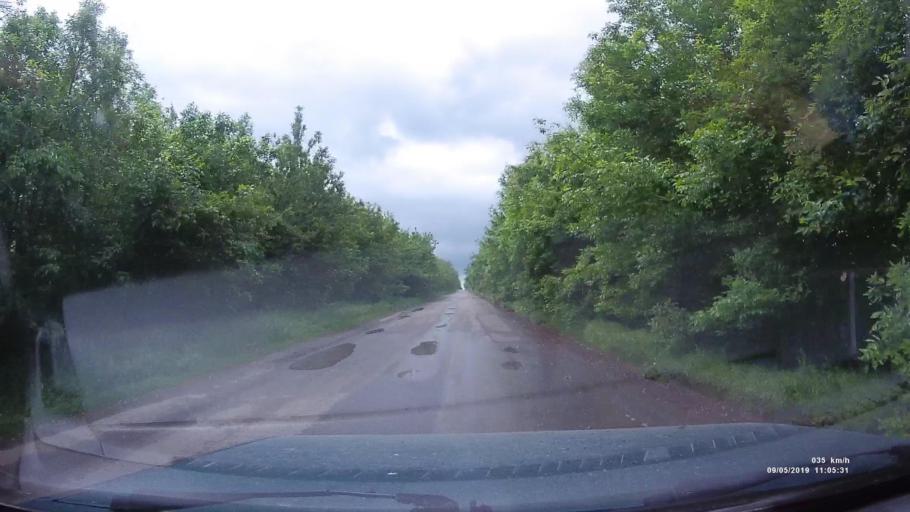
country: RU
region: Krasnodarskiy
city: Kanelovskaya
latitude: 46.8095
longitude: 39.2098
